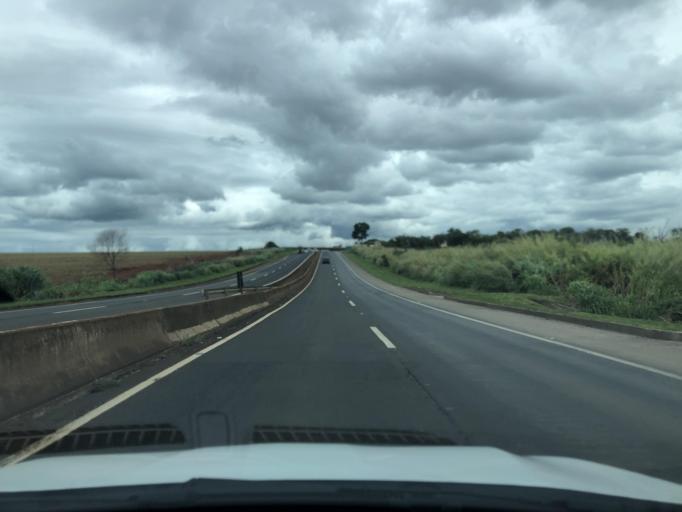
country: BR
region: Sao Paulo
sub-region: Igarapava
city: Igarapava
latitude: -19.9644
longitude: -47.7959
